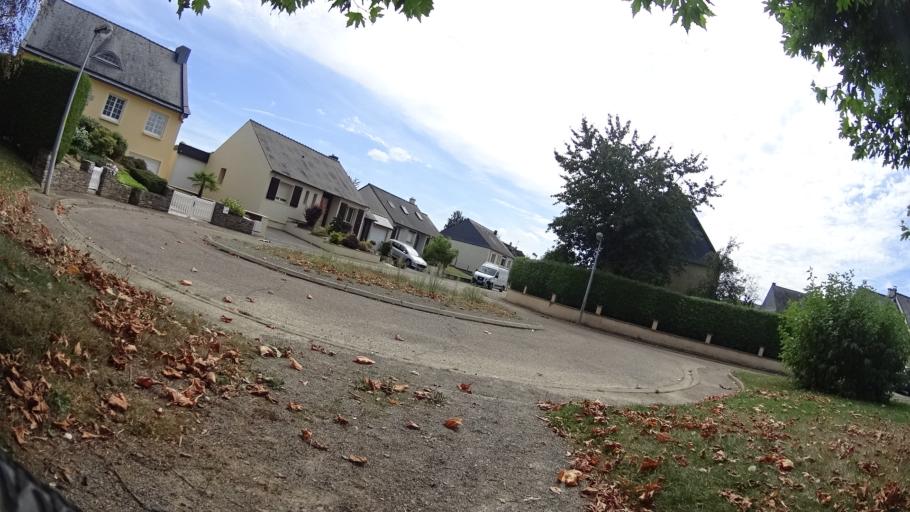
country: FR
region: Brittany
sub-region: Departement d'Ille-et-Vilaine
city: La Meziere
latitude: 48.2207
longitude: -1.7533
